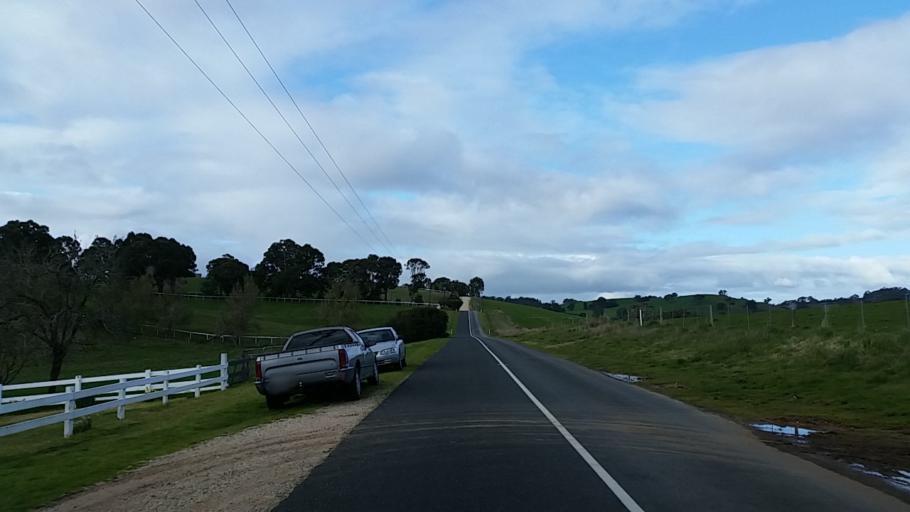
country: AU
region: South Australia
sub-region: Mount Barker
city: Hahndorf
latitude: -35.0185
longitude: 138.8132
